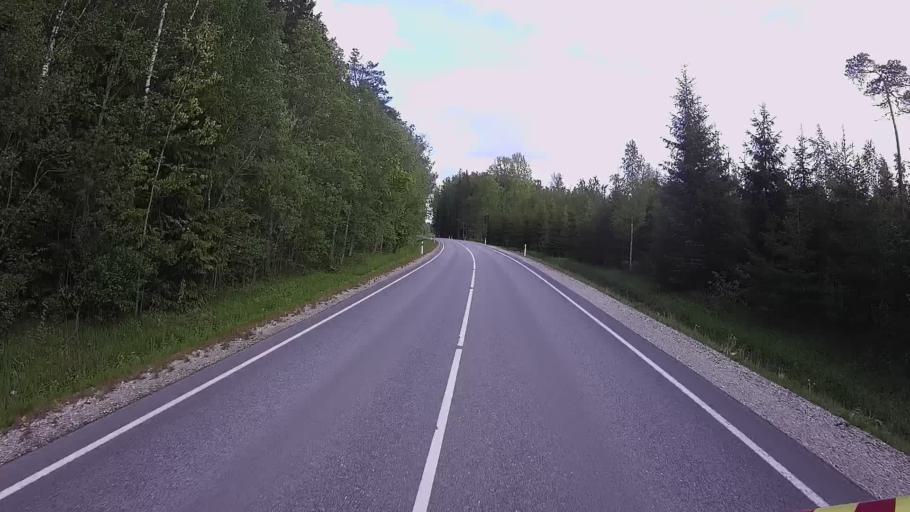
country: EE
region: Jogevamaa
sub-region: Mustvee linn
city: Mustvee
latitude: 58.8716
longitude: 26.8240
